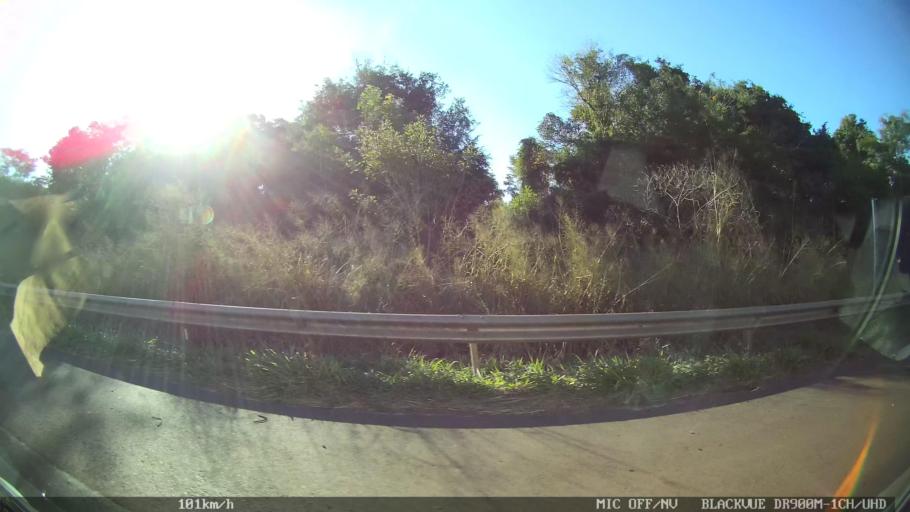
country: BR
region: Sao Paulo
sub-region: Guapiacu
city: Guapiacu
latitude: -20.7432
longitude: -49.1059
